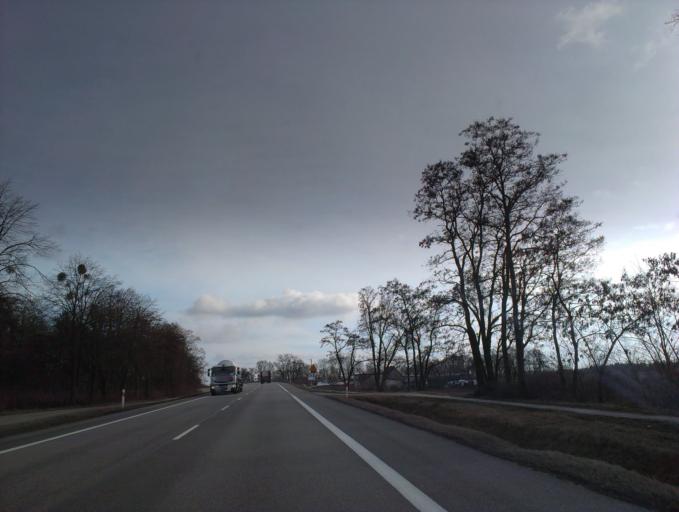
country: PL
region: Kujawsko-Pomorskie
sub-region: Powiat lipnowski
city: Lipno
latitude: 52.8566
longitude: 19.1603
